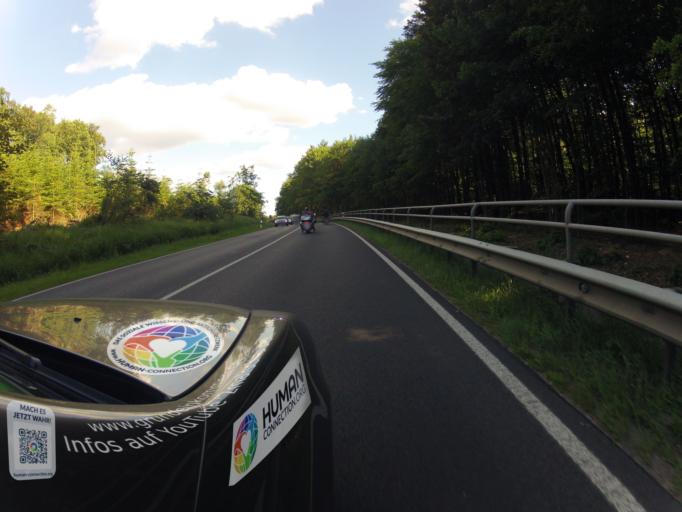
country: DE
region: Mecklenburg-Vorpommern
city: Seebad Bansin
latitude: 53.9700
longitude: 14.1187
